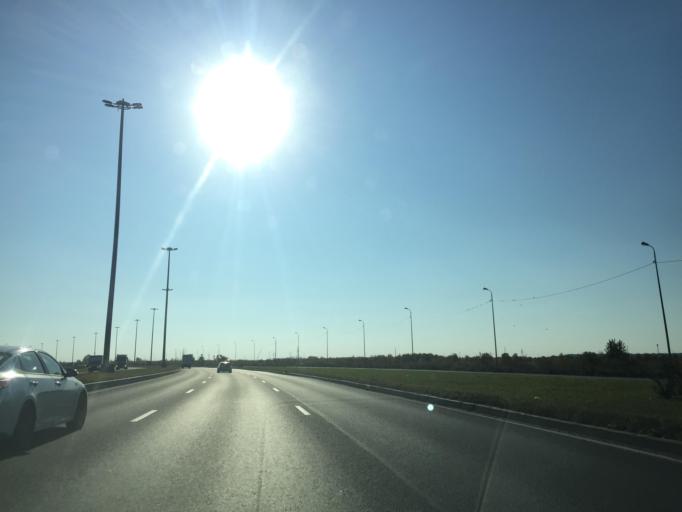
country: RU
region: St.-Petersburg
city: Petro-Slavyanka
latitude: 59.7685
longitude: 30.5007
